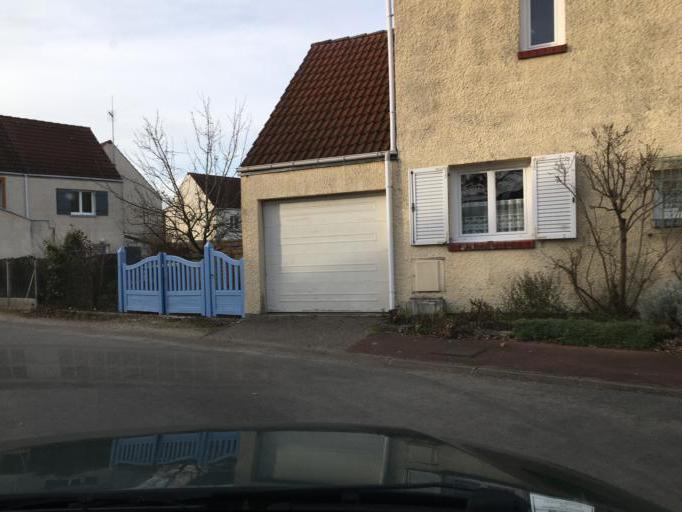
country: FR
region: Centre
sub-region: Departement du Loiret
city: La Ferte-Saint-Aubin
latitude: 47.7178
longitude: 1.9397
